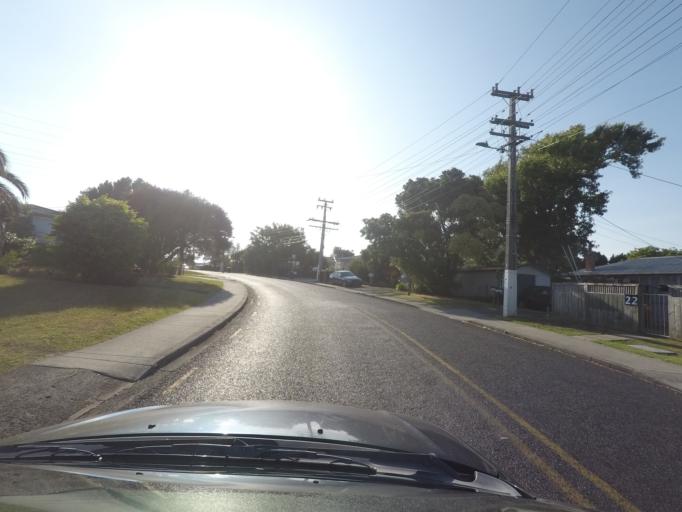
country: NZ
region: Auckland
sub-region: Auckland
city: Rosebank
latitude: -36.8565
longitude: 174.6452
